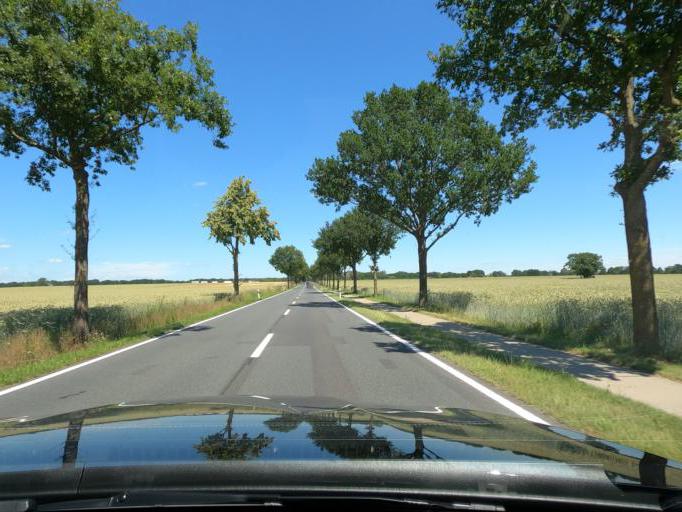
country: DE
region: Lower Saxony
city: Burgdorf
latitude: 52.4276
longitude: 9.9824
